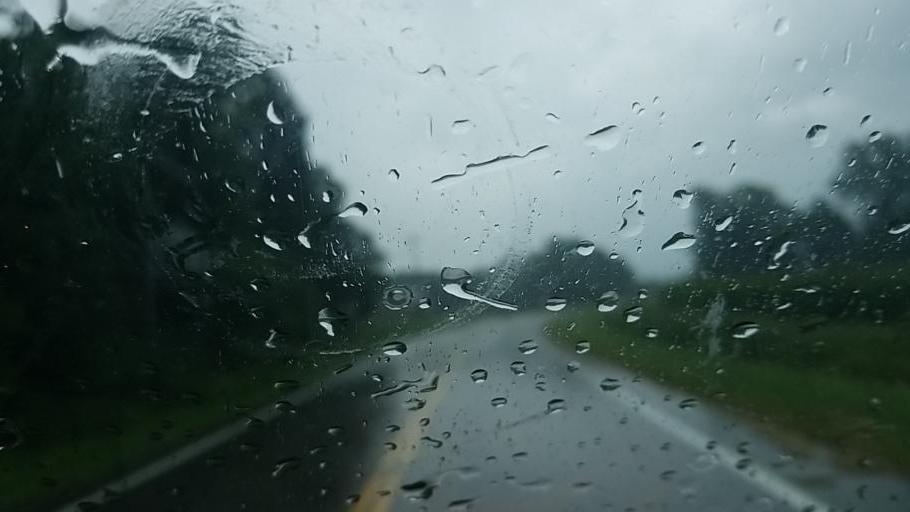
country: US
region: Ohio
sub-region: Logan County
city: Bellefontaine
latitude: 40.3279
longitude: -83.6619
